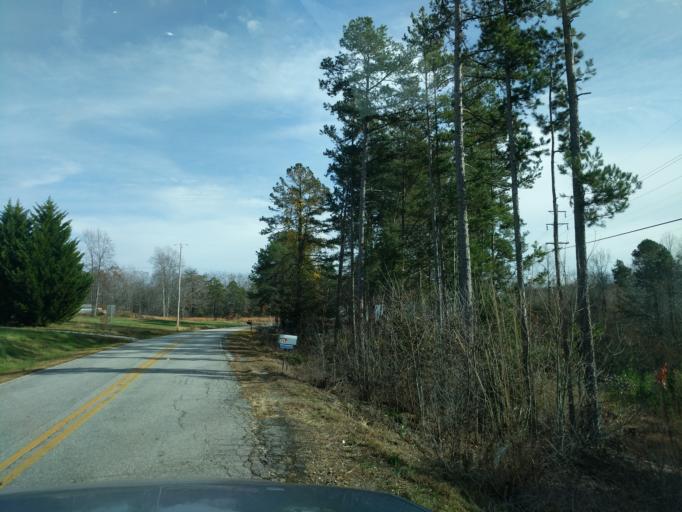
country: US
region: South Carolina
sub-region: Oconee County
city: Walhalla
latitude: 34.8344
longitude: -83.0559
